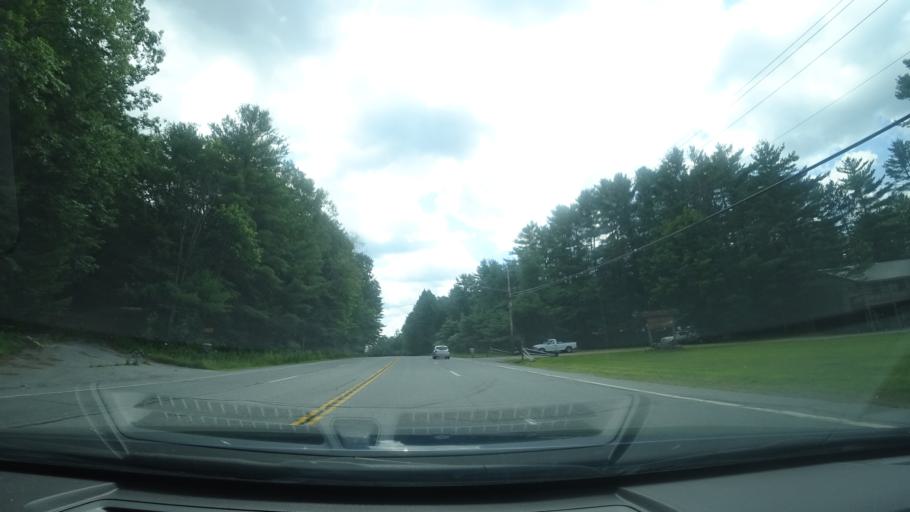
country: US
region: New York
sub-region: Warren County
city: Warrensburg
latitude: 43.5144
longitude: -73.7916
